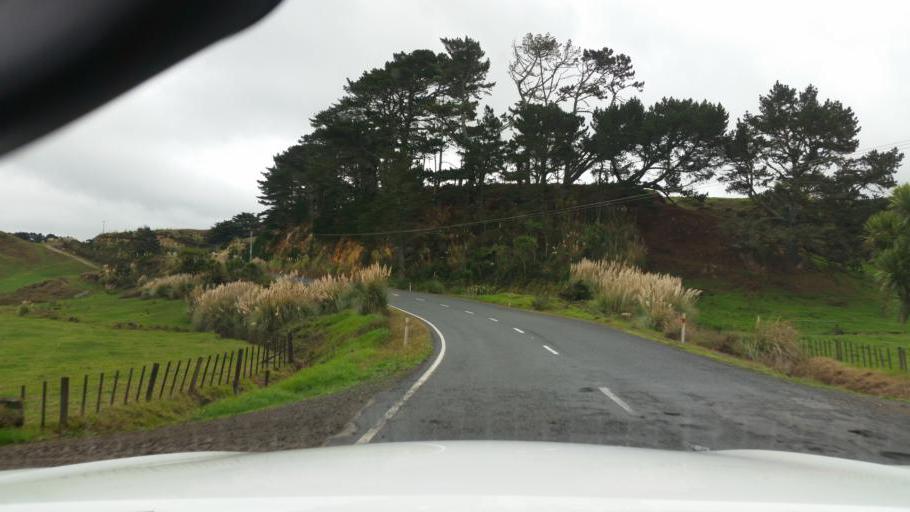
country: NZ
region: Northland
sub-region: Kaipara District
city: Dargaville
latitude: -36.1593
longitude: 173.9888
